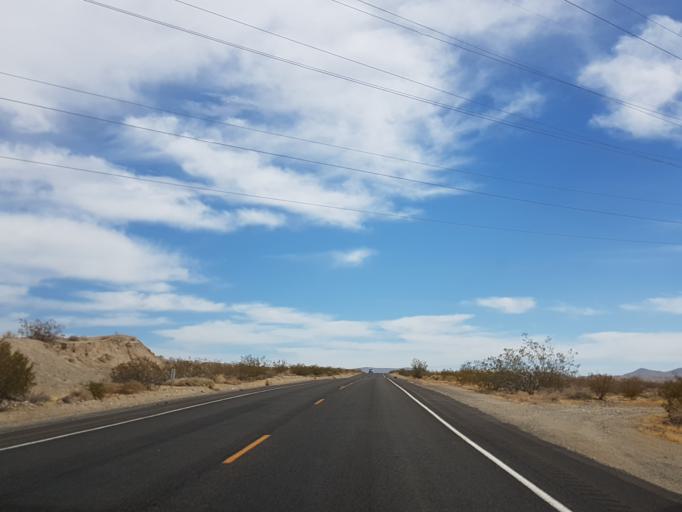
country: US
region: California
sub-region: Kern County
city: Ridgecrest
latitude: 35.4263
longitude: -117.6995
